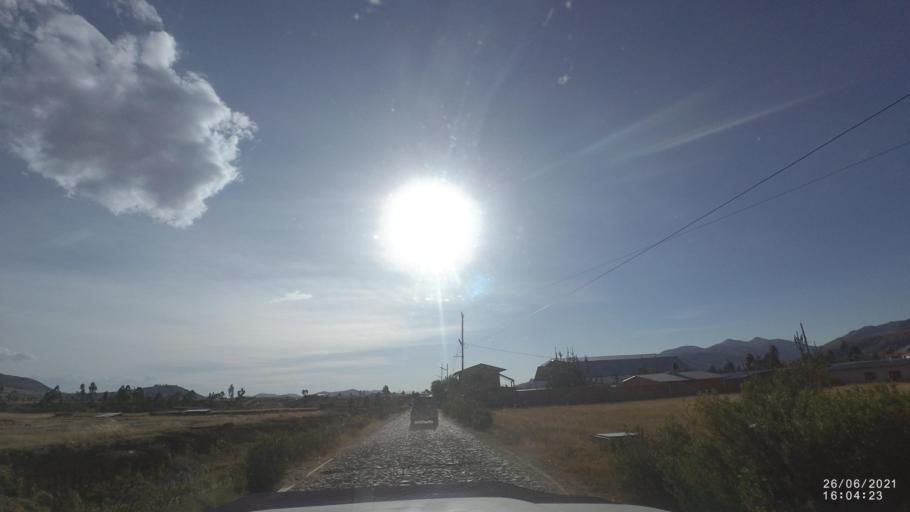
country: BO
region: Cochabamba
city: Arani
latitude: -17.8323
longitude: -65.7562
